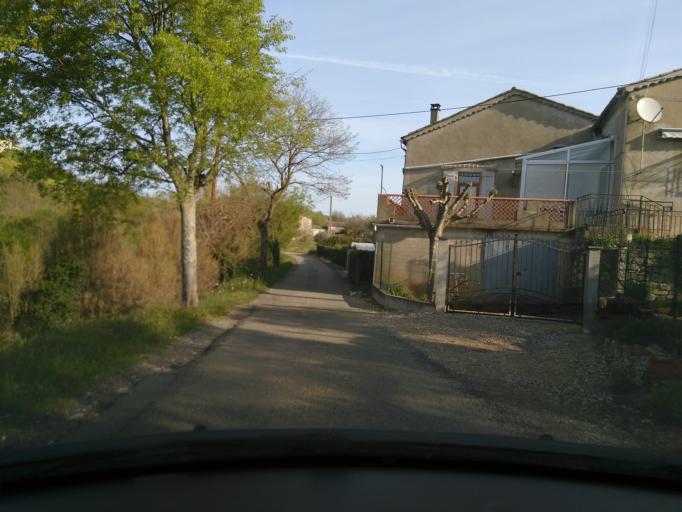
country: FR
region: Rhone-Alpes
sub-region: Departement de l'Ardeche
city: Ruoms
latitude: 44.4496
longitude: 4.4196
